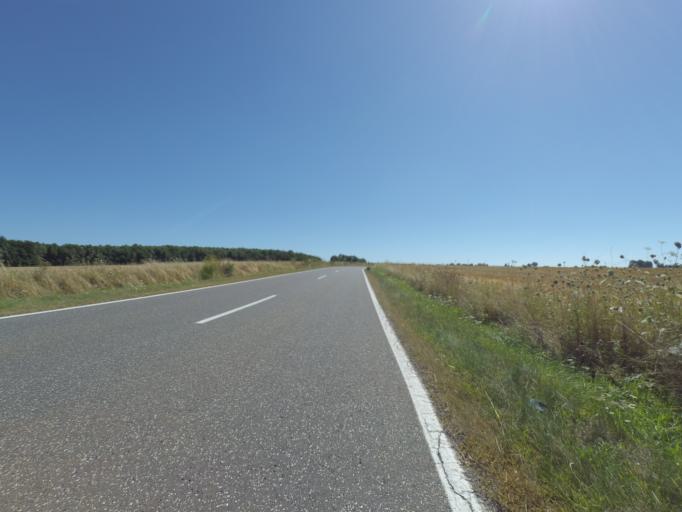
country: DE
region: Rheinland-Pfalz
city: Beuren
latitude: 50.1029
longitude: 7.0706
